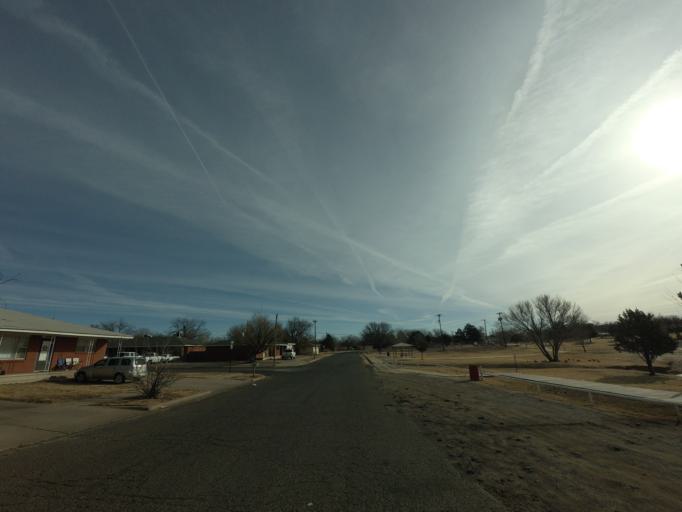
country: US
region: New Mexico
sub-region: Curry County
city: Clovis
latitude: 34.4135
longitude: -103.2195
